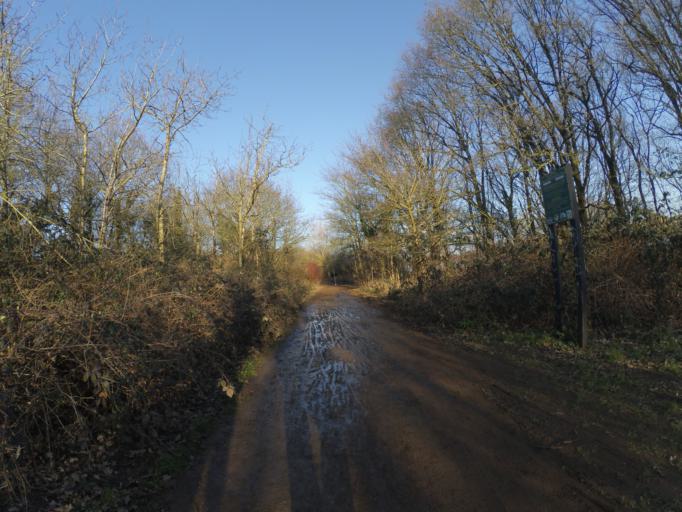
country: GB
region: England
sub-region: Greater London
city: Hendon
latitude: 51.5716
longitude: -0.2481
